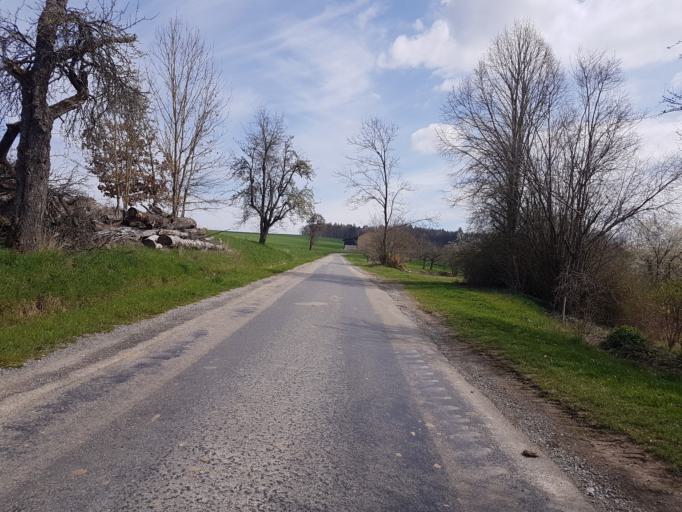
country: DE
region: Baden-Wuerttemberg
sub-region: Regierungsbezirk Stuttgart
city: Forchtenberg
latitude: 49.3699
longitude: 9.5467
